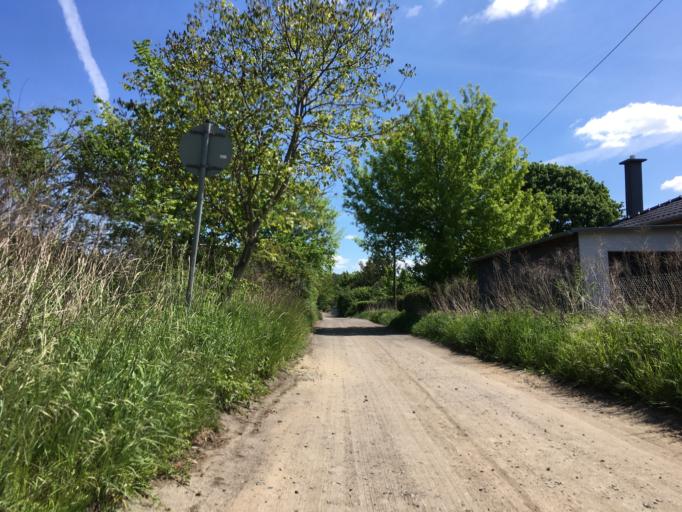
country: DE
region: Brandenburg
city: Eberswalde
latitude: 52.8423
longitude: 13.8270
